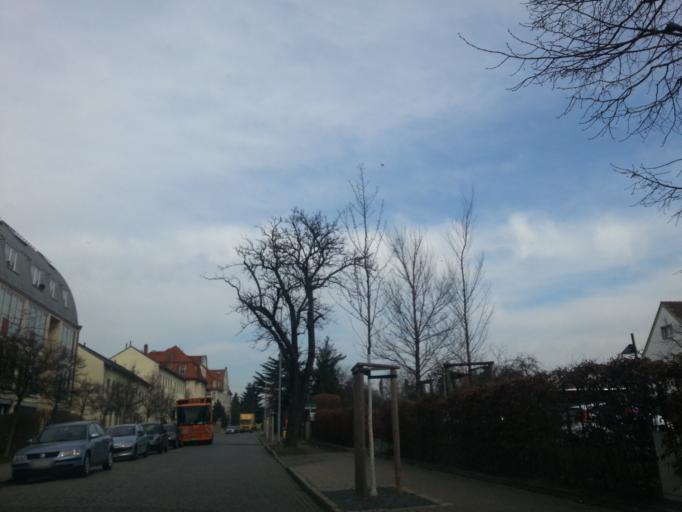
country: DE
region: Saxony
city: Dresden
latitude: 51.0806
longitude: 13.7326
